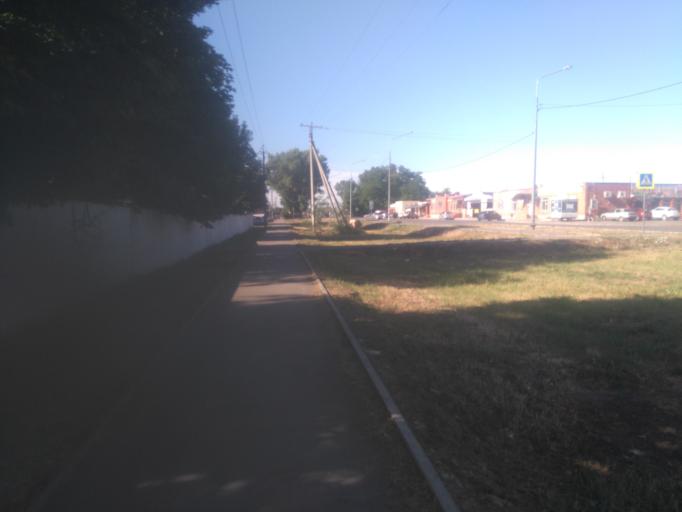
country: RU
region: Krasnodarskiy
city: Fastovetskaya
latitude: 45.9115
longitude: 40.1525
